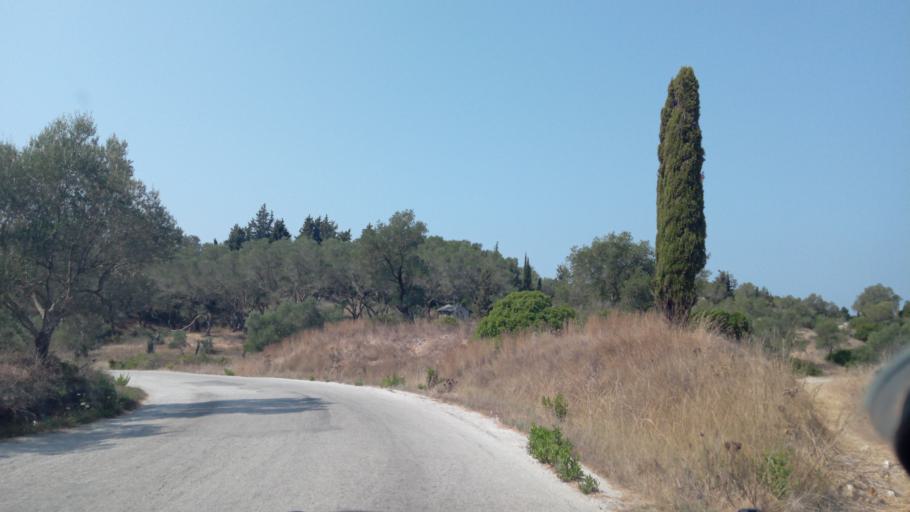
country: GR
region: Ionian Islands
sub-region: Nomos Kerkyras
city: Perivoli
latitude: 39.4173
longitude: 20.0308
